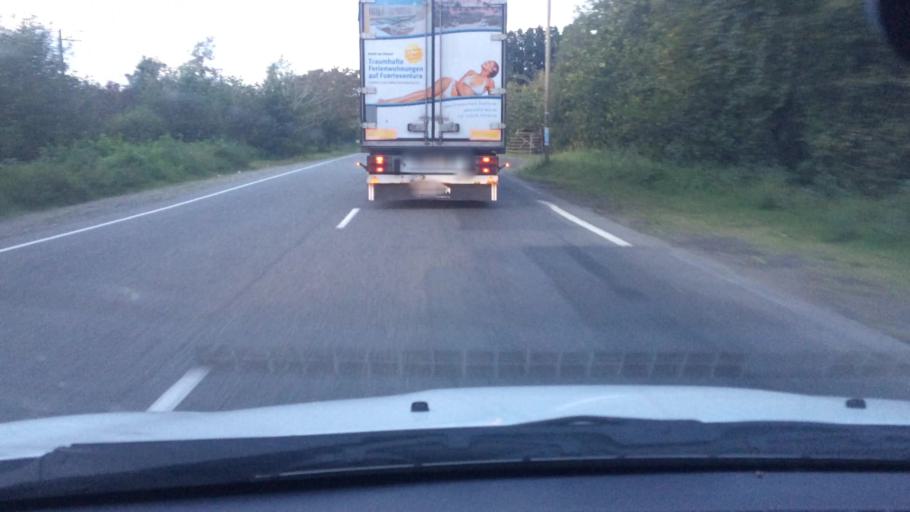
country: GE
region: Guria
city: Urek'i
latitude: 41.9805
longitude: 41.7829
